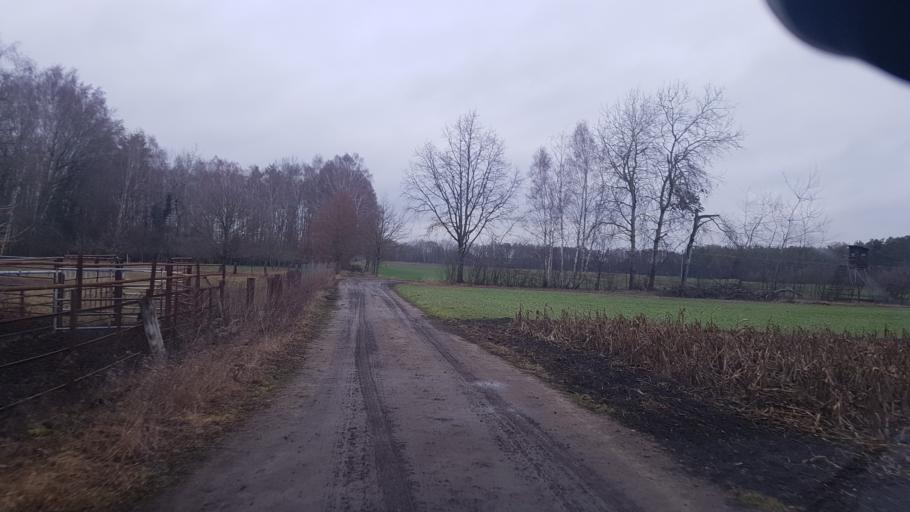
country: DE
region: Brandenburg
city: Ruckersdorf
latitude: 51.6004
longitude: 13.5931
